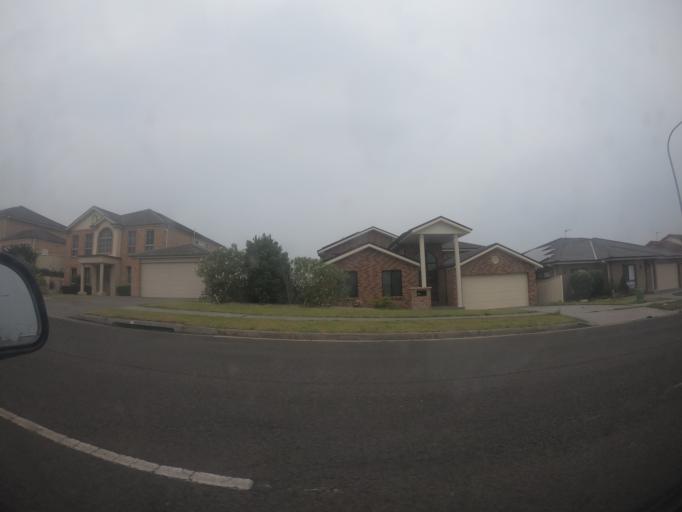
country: AU
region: New South Wales
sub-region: Shellharbour
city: Flinders
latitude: -34.5762
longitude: 150.8419
